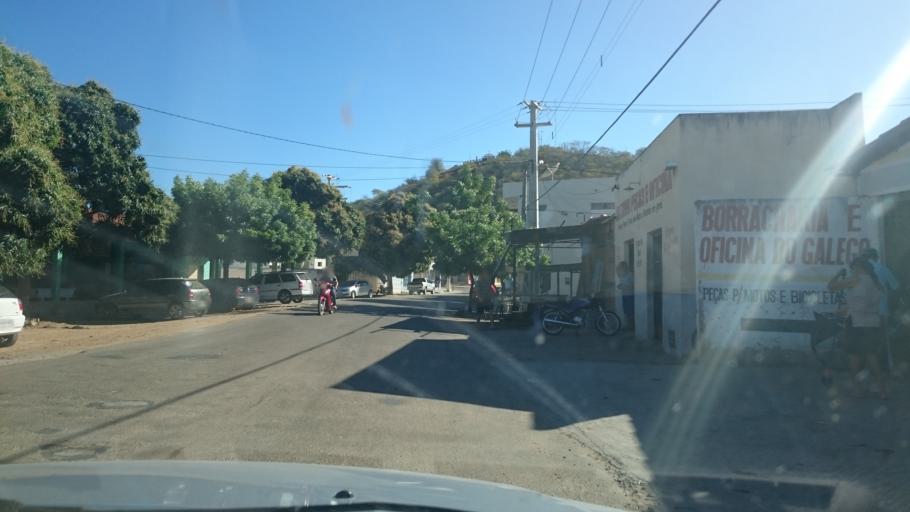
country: BR
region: Paraiba
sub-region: Catole Do Rocha
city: Sao Bento
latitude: -6.1549
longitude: -37.7650
